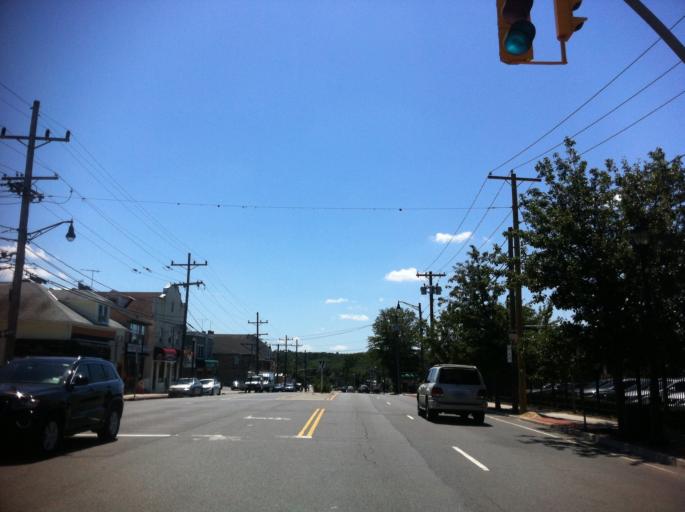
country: US
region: New York
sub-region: Nassau County
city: Glen Cove
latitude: 40.8571
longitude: -73.6199
